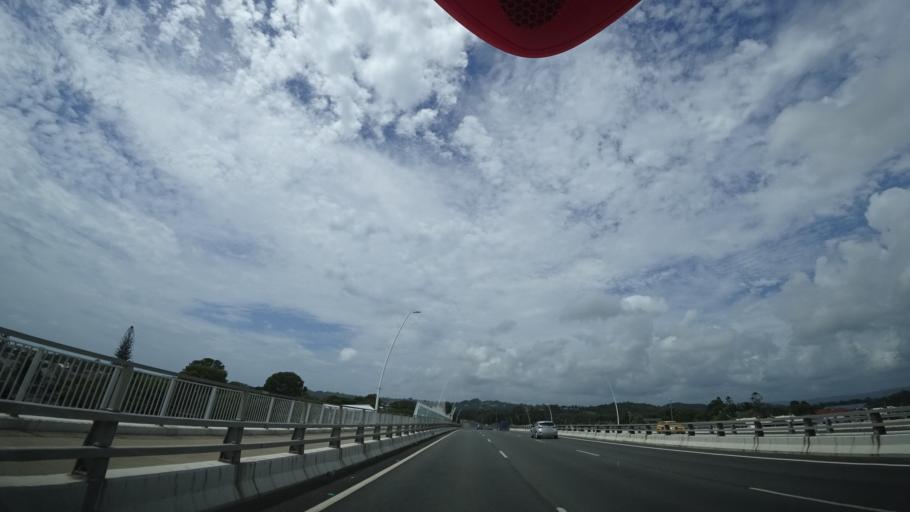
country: AU
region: Queensland
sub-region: Sunshine Coast
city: Buderim
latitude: -26.6418
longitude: 153.0678
